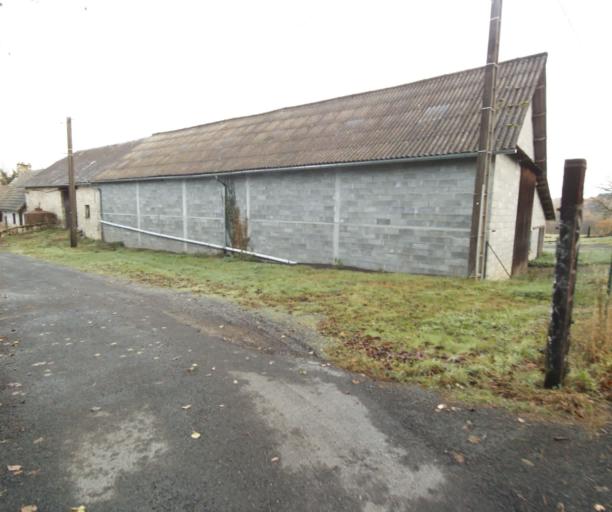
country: FR
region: Limousin
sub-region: Departement de la Correze
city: Cornil
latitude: 45.2116
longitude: 1.7156
